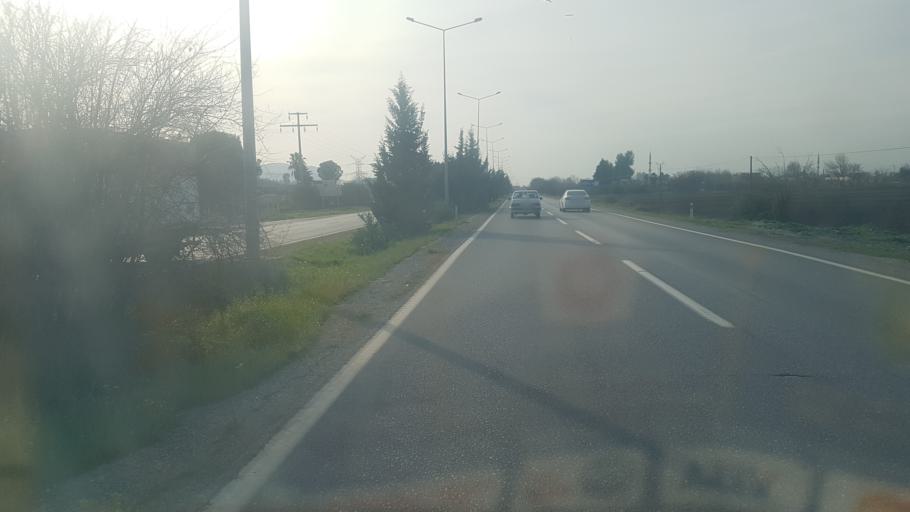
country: TR
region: Osmaniye
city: Toprakkale
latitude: 37.0548
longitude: 36.1337
